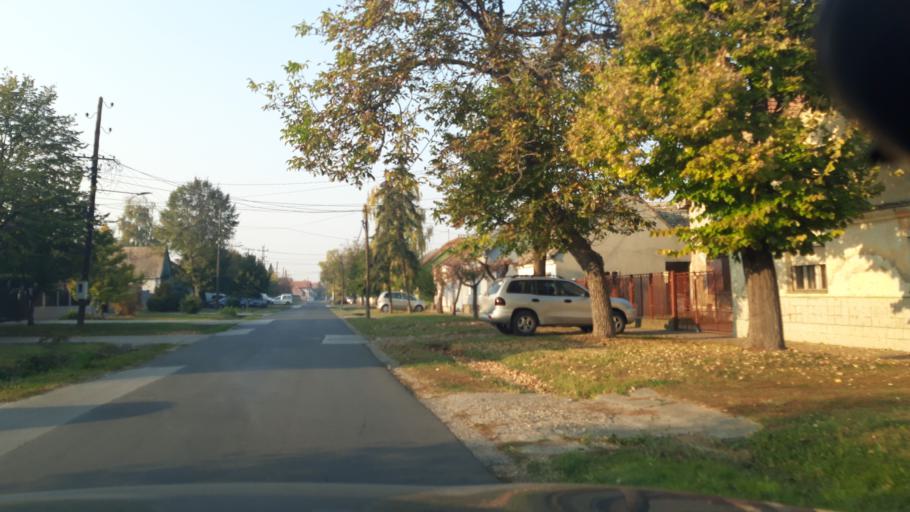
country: RS
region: Autonomna Pokrajina Vojvodina
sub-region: Sremski Okrug
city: Stara Pazova
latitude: 44.9933
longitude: 20.1468
